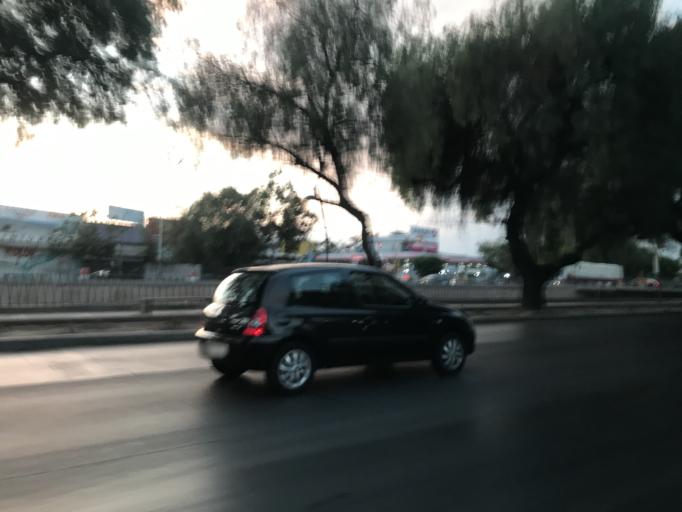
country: AR
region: Mendoza
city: Mendoza
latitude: -32.8908
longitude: -68.8304
